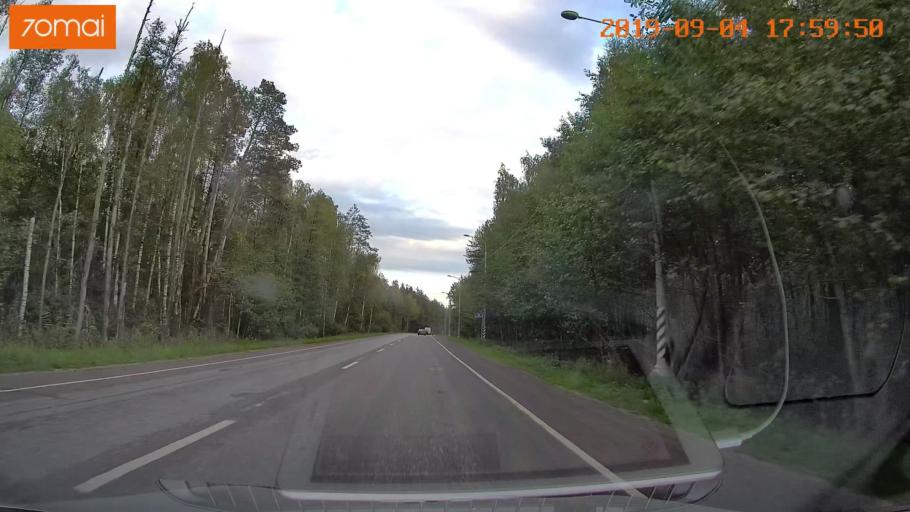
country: RU
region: Moskovskaya
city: Il'inskiy Pogost
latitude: 55.4919
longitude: 38.8491
